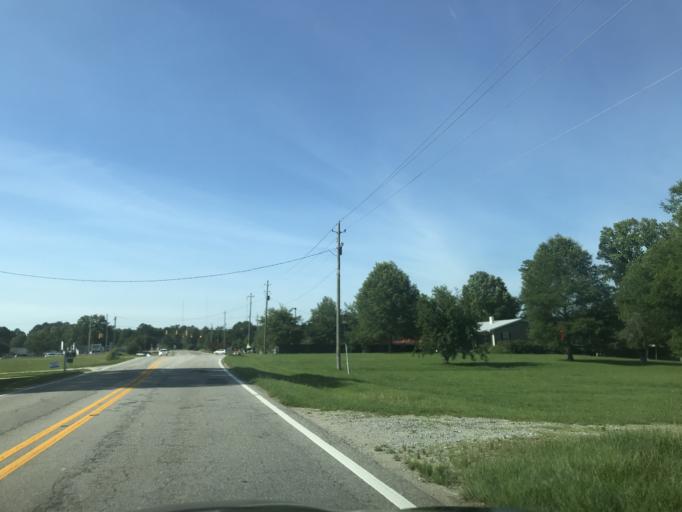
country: US
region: North Carolina
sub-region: Johnston County
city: Clayton
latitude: 35.6152
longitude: -78.5356
